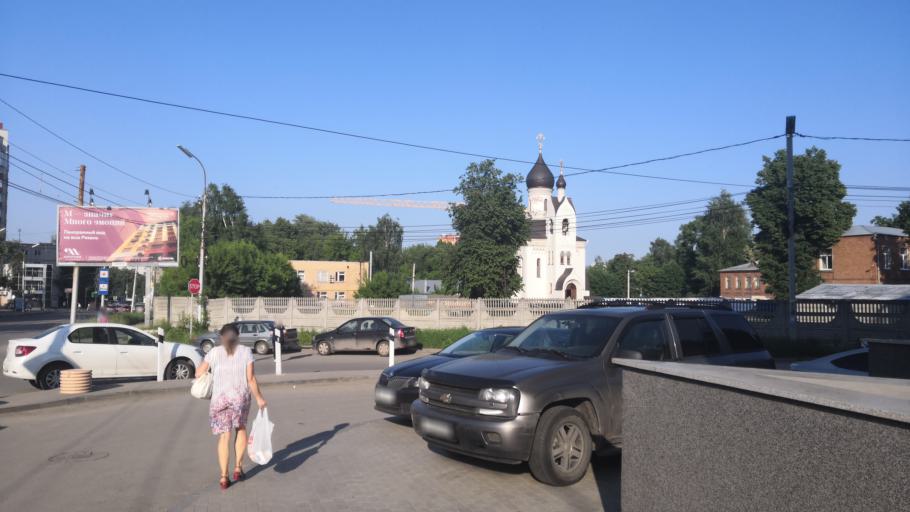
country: RU
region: Rjazan
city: Ryazan'
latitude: 54.6175
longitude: 39.7312
